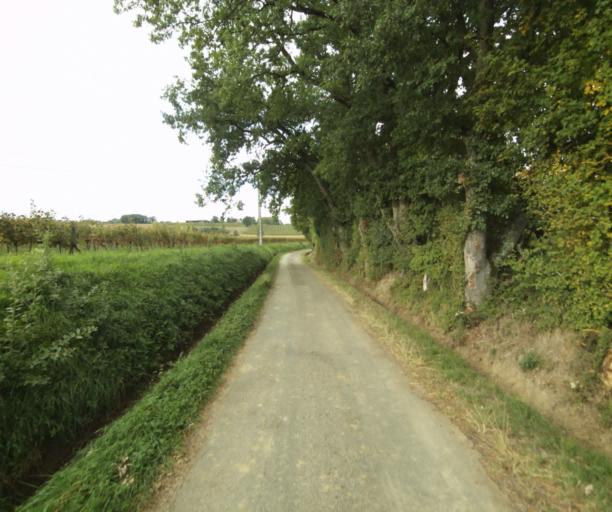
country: FR
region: Midi-Pyrenees
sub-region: Departement du Gers
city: Gondrin
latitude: 43.8598
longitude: 0.2705
